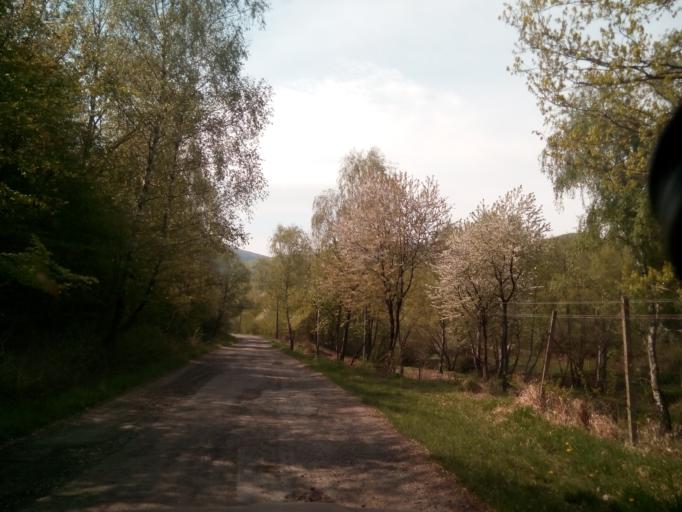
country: SK
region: Presovsky
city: Giraltovce
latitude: 48.9727
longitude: 21.5051
